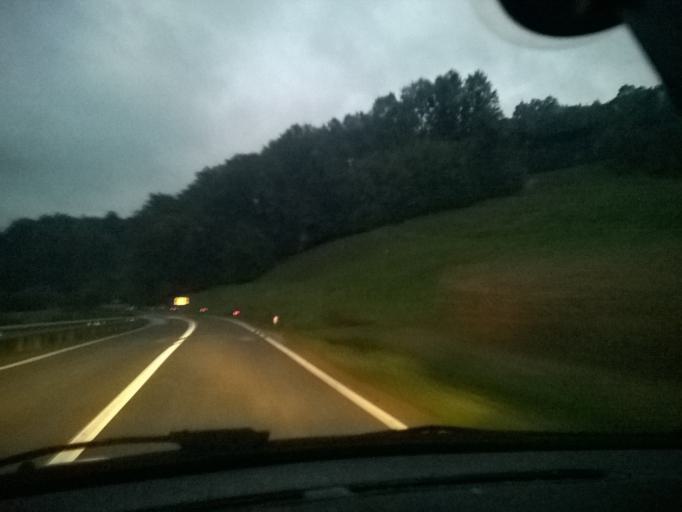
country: SI
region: Rogatec
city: Rogatec
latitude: 46.2177
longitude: 15.7290
